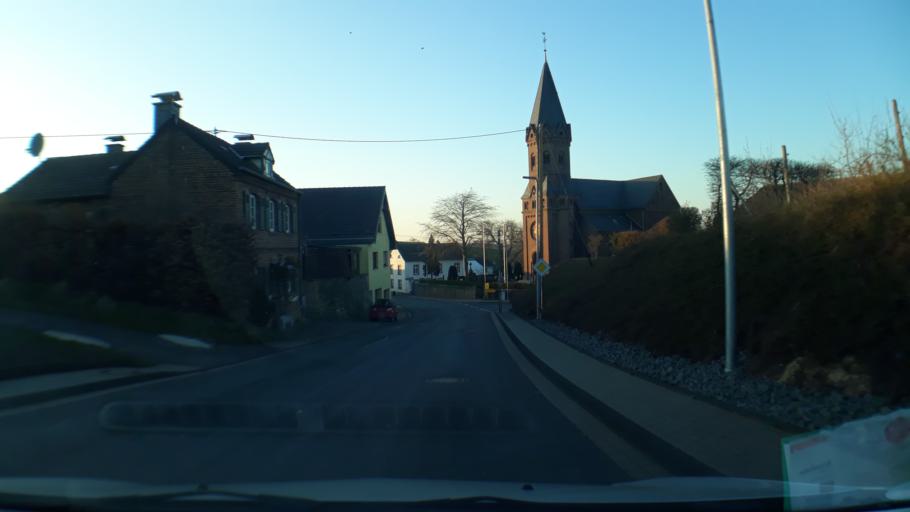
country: DE
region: North Rhine-Westphalia
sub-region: Regierungsbezirk Koln
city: Mechernich
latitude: 50.6348
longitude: 6.6135
